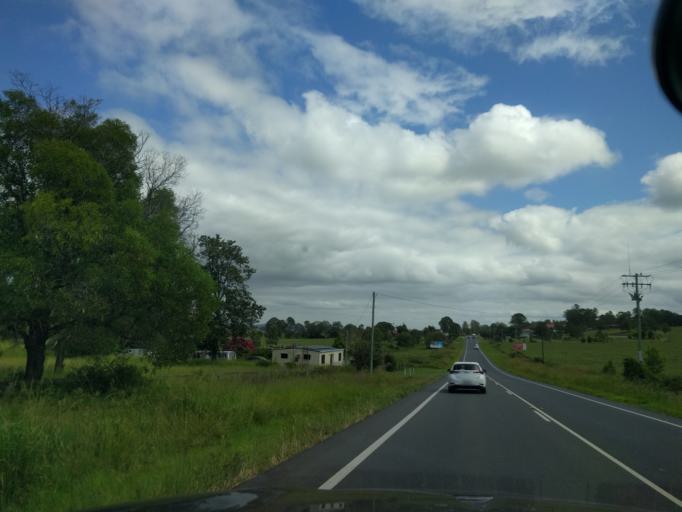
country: AU
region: Queensland
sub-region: Logan
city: Cedar Vale
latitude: -27.8988
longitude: 152.9746
